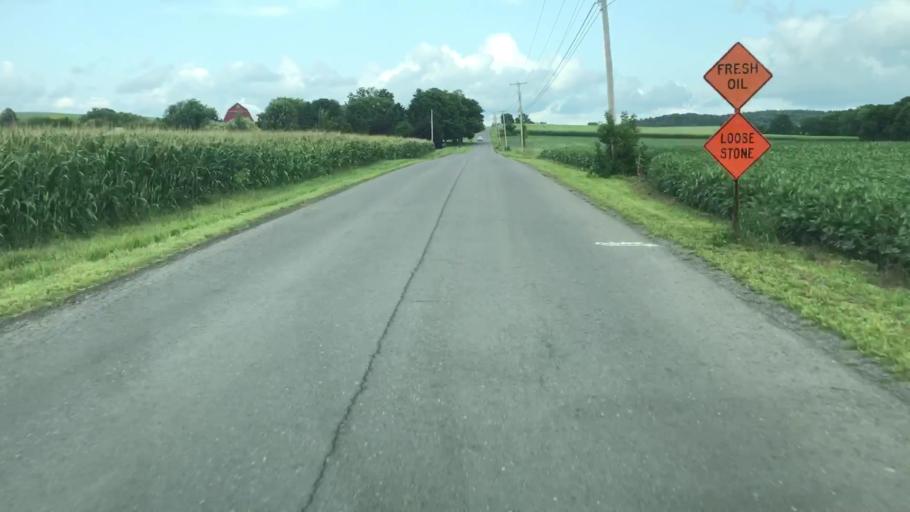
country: US
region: New York
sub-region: Onondaga County
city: Elbridge
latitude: 42.9850
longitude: -76.5058
